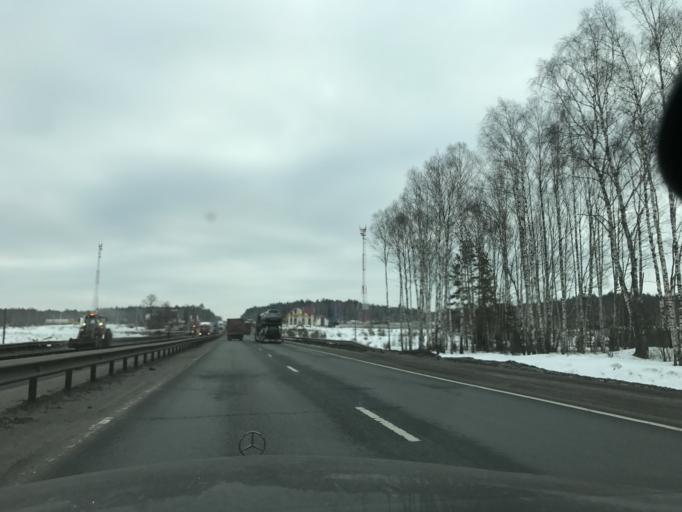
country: RU
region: Vladimir
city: Stepantsevo
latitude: 56.2301
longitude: 41.7283
